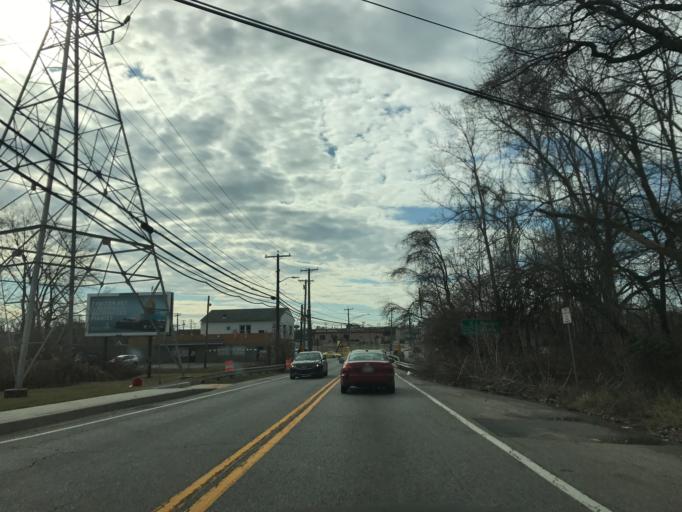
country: US
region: Maryland
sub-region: Anne Arundel County
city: Glen Burnie
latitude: 39.1838
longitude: -76.6143
